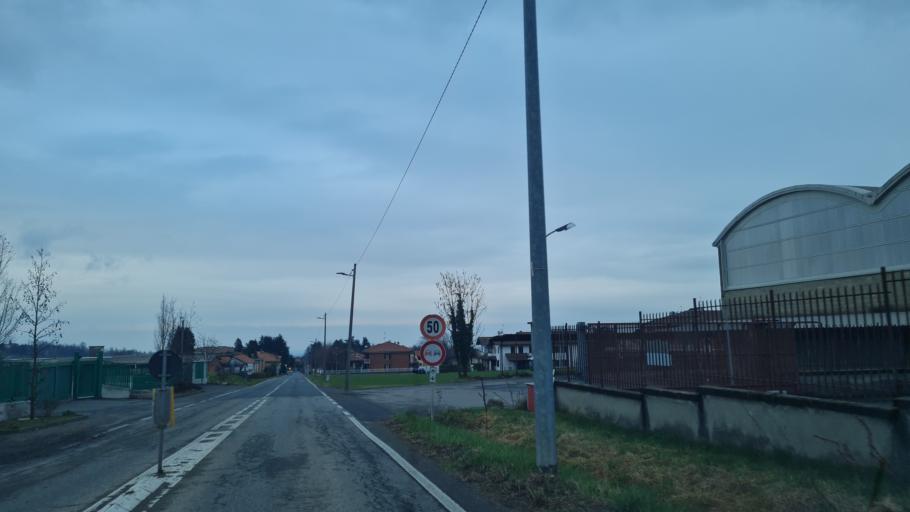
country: IT
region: Piedmont
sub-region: Provincia di Biella
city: Muzzano
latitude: 45.5667
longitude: 7.9953
